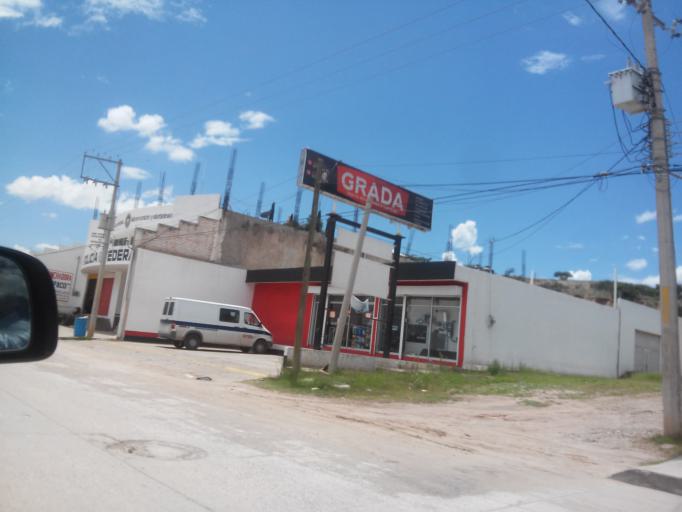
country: MX
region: Durango
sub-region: Santiago Papasquiaro
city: Santiago Papasquiaro
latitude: 25.0571
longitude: -105.4255
